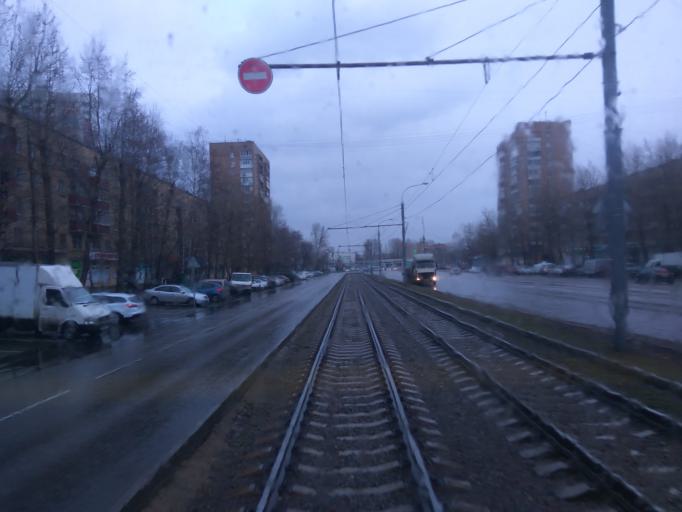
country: RU
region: Moscow
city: Kozeyevo
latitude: 55.8760
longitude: 37.6365
